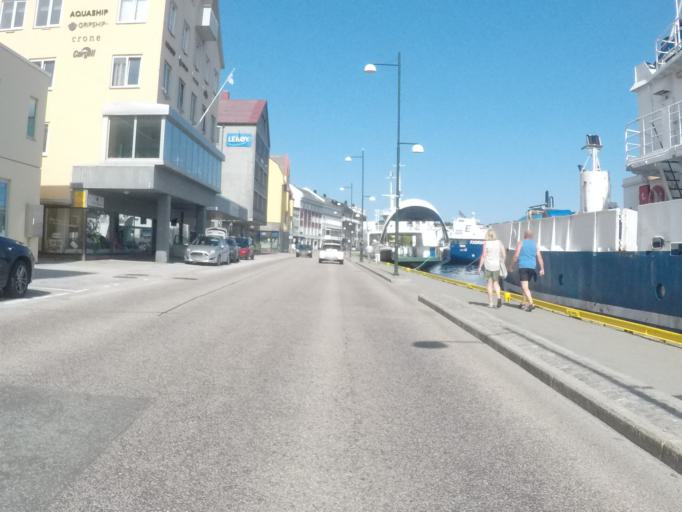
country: NO
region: More og Romsdal
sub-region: Kristiansund
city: Kristiansund
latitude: 63.1122
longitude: 7.7328
